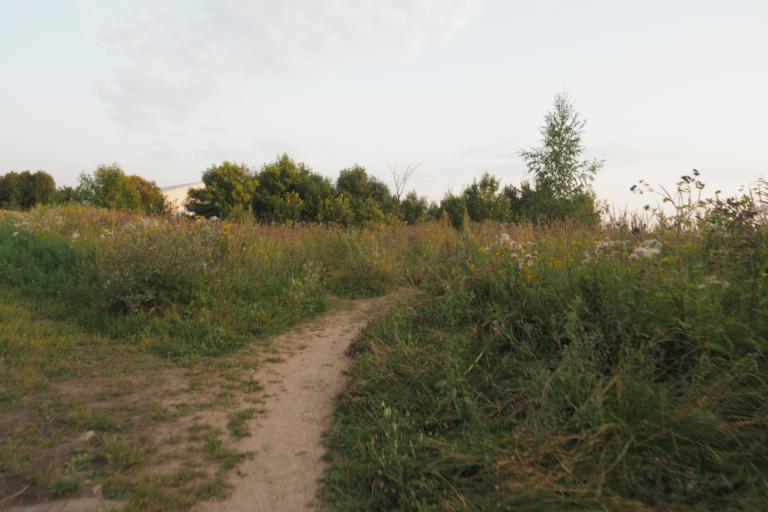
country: RU
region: Moscow
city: Orekhovo-Borisovo
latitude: 55.6020
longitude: 37.7054
